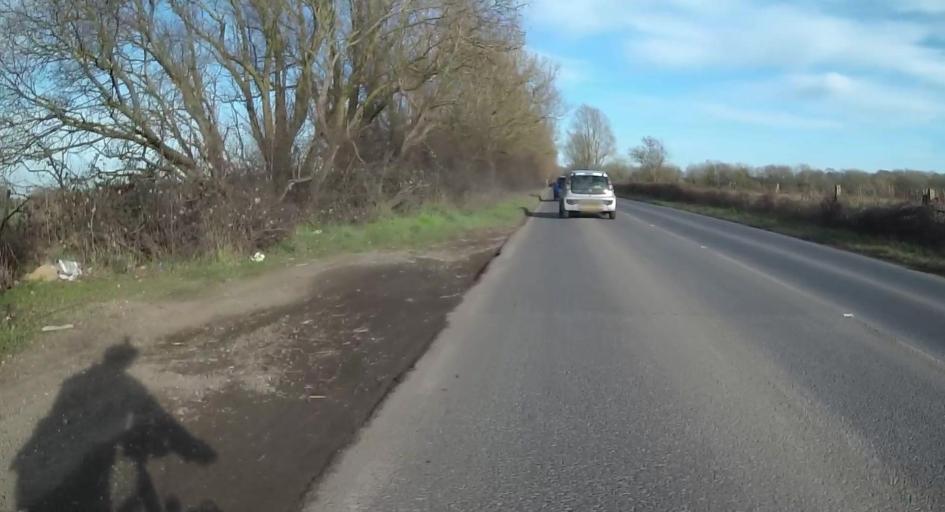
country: GB
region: England
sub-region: Wokingham
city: Swallowfield
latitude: 51.4016
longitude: -0.9889
